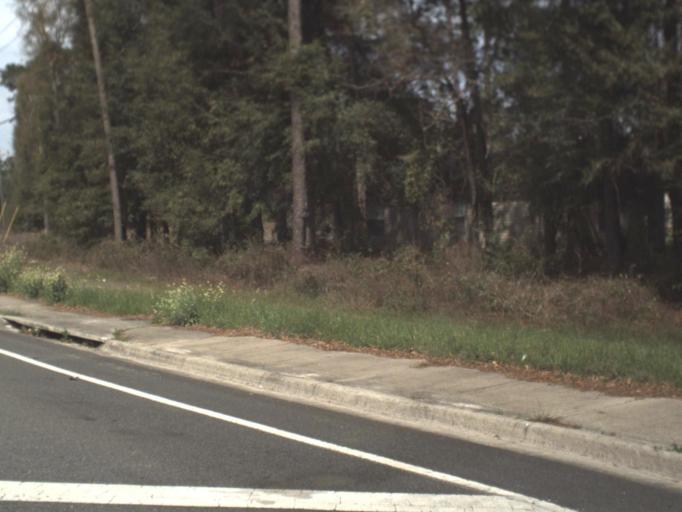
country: US
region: Florida
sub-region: Leon County
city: Tallahassee
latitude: 30.3762
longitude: -84.2973
